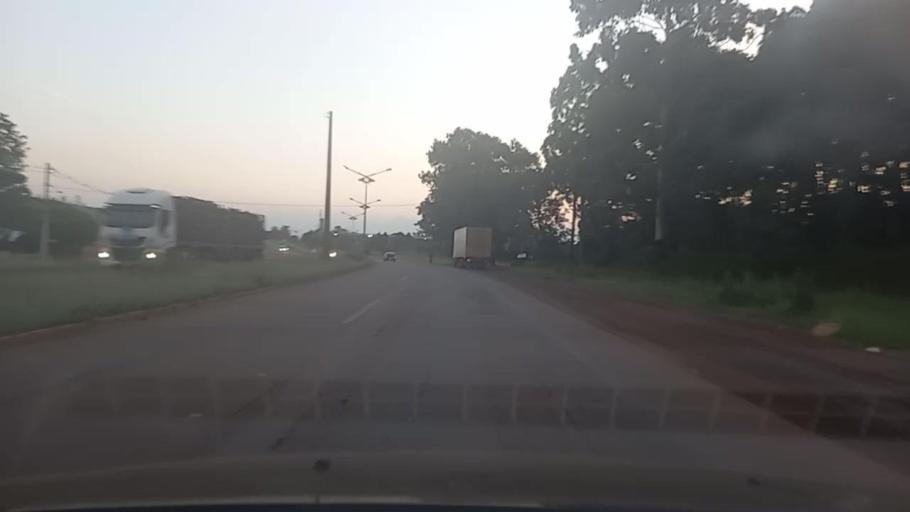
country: BR
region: Rio Grande do Sul
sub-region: Passo Fundo
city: Passo Fundo
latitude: -28.2758
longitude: -52.4490
